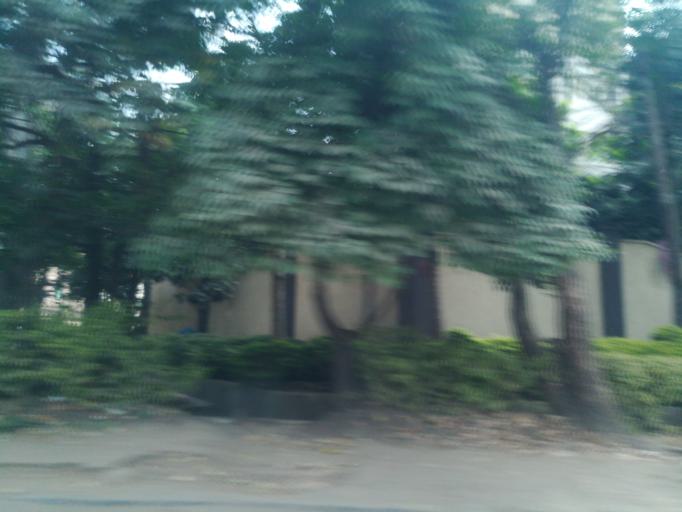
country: KE
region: Nairobi Area
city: Nairobi
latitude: -1.2903
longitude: 36.7904
